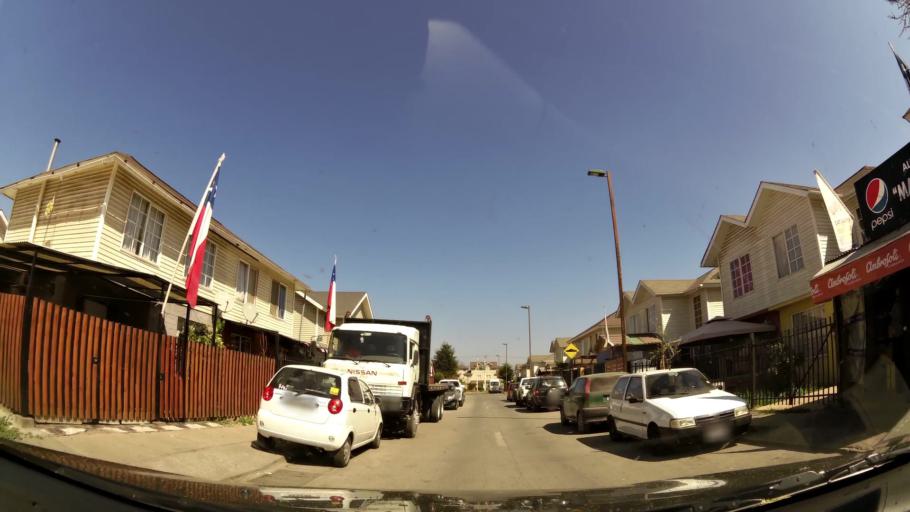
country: CL
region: Santiago Metropolitan
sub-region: Provincia de Chacabuco
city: Chicureo Abajo
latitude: -33.3299
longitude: -70.7475
